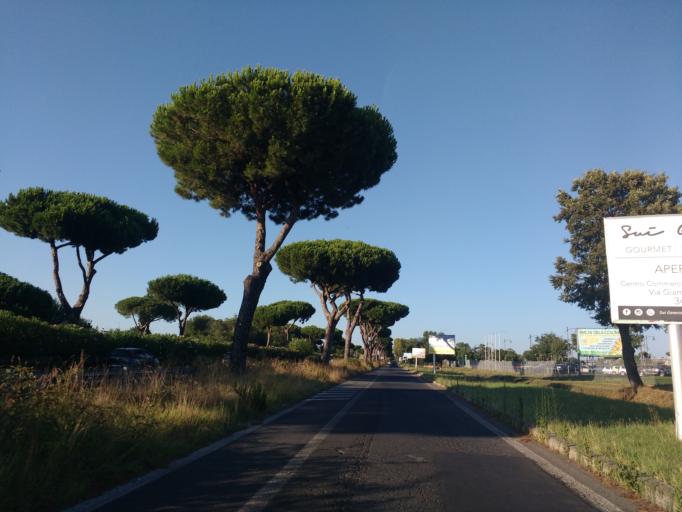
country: IT
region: Latium
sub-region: Citta metropolitana di Roma Capitale
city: Acilia-Castel Fusano-Ostia Antica
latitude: 41.7522
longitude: 12.3664
